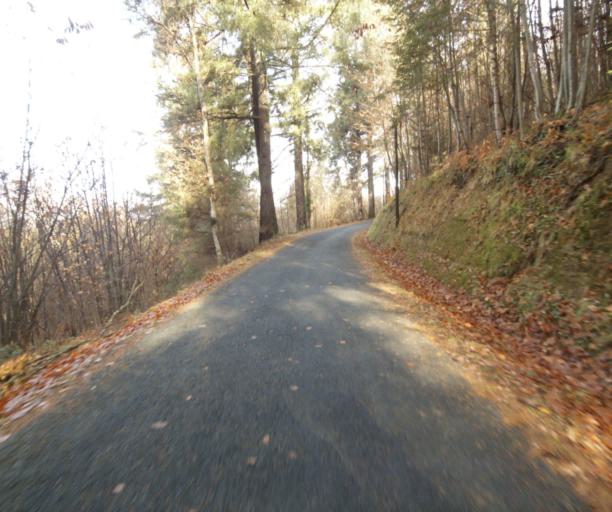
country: FR
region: Limousin
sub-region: Departement de la Correze
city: Sainte-Fortunade
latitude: 45.2174
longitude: 1.7461
